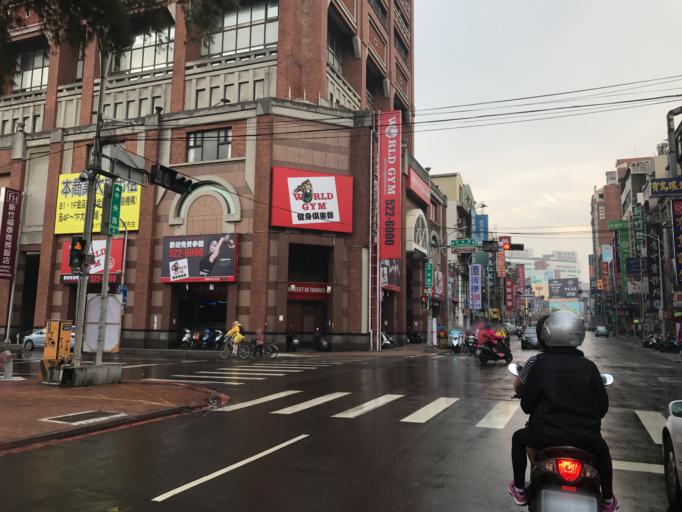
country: TW
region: Taiwan
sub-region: Hsinchu
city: Hsinchu
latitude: 24.8061
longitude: 120.9690
